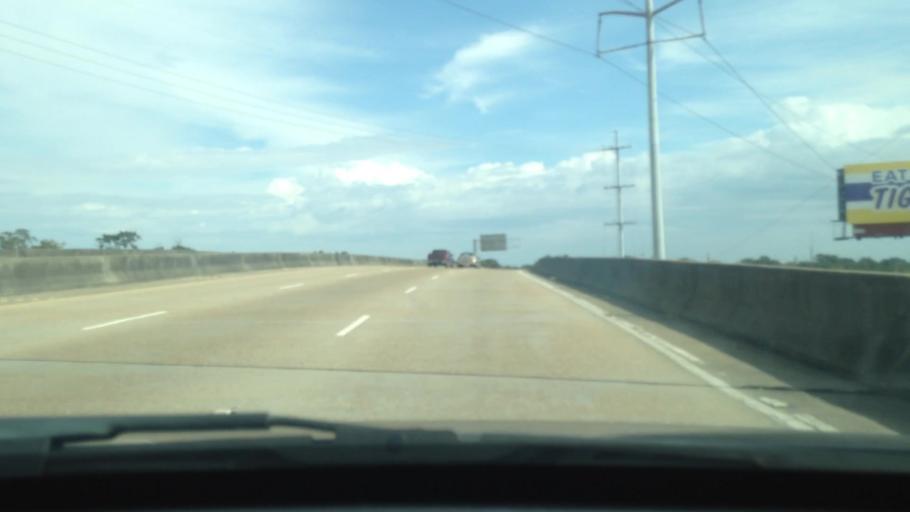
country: US
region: Louisiana
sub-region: Jefferson Parish
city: Metairie Terrace
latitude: 29.9708
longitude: -90.1735
